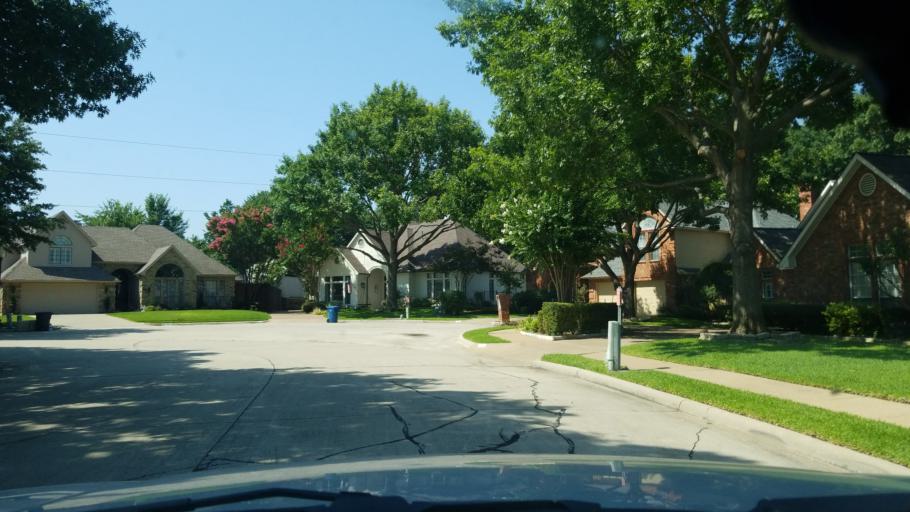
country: US
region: Texas
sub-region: Dallas County
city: Coppell
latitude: 32.9537
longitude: -96.9856
